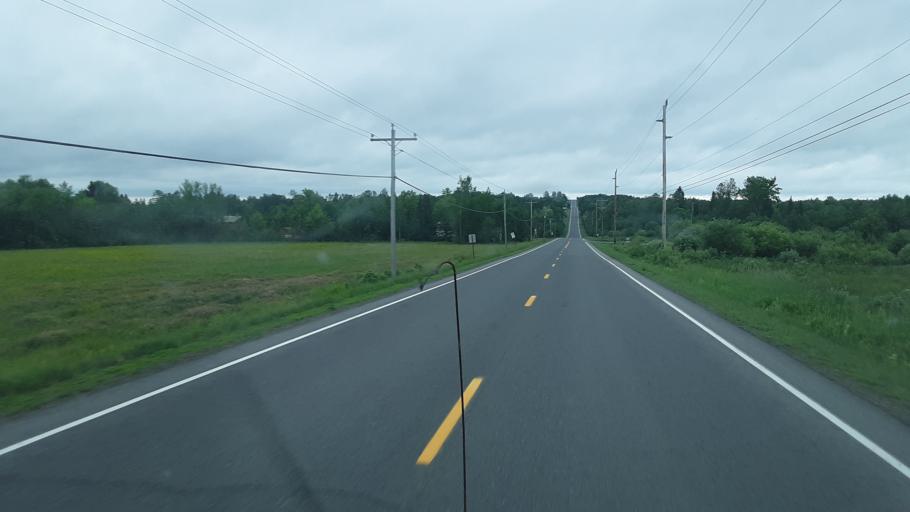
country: US
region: Maine
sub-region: Penobscot County
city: Patten
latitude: 45.9691
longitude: -68.4510
